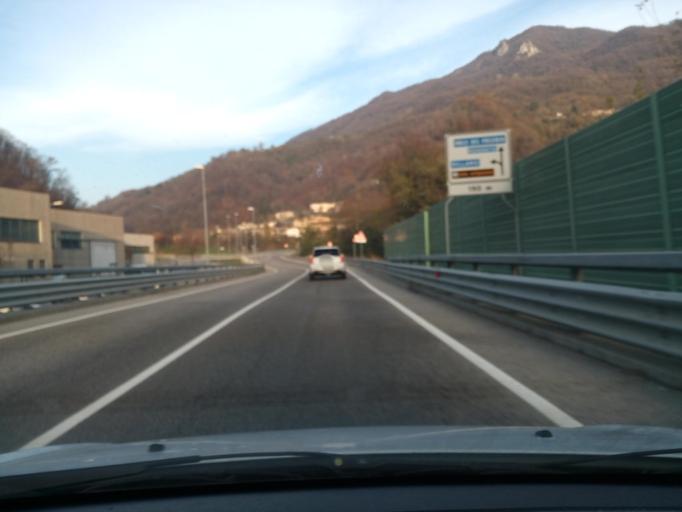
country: IT
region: Veneto
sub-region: Provincia di Vicenza
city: Torrebelvicino
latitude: 45.7163
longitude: 11.3084
